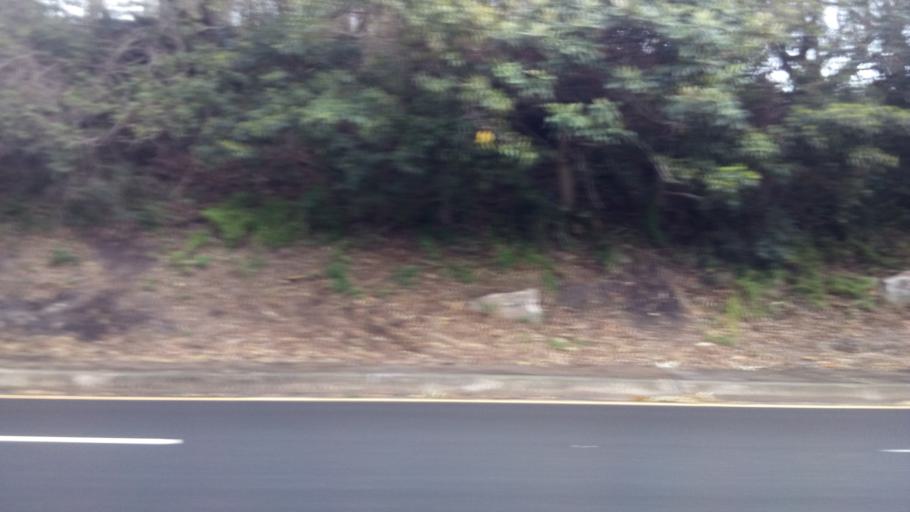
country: AU
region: New South Wales
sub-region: Wollongong
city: Corrimal
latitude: -34.3633
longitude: 150.8990
